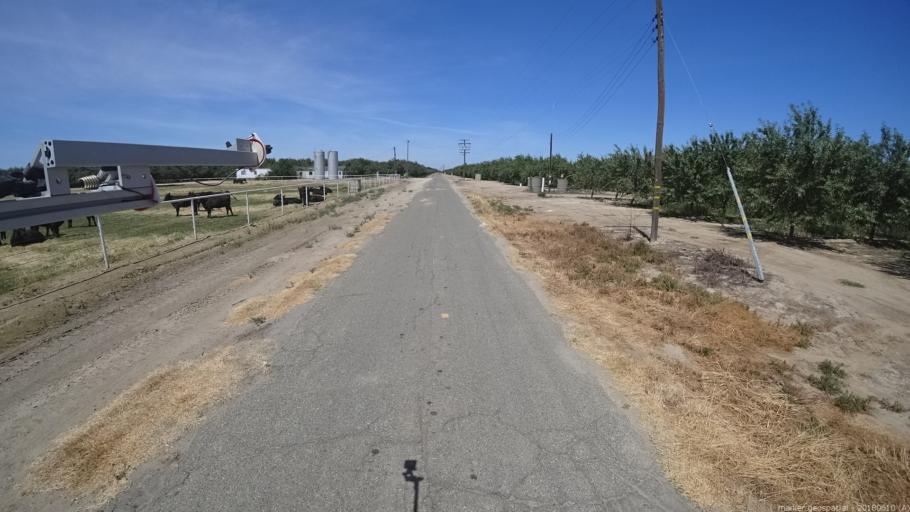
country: US
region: California
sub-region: Madera County
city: Chowchilla
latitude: 37.0471
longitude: -120.4030
